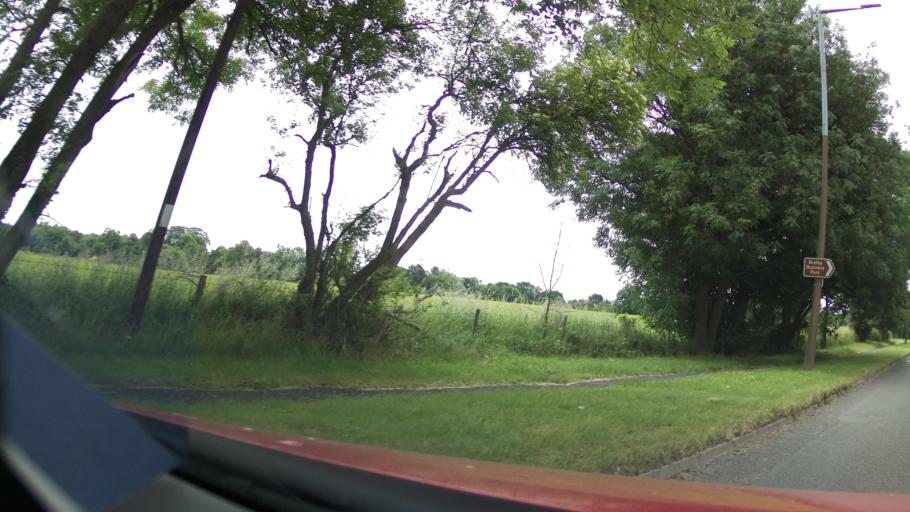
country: GB
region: England
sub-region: Derbyshire
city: Swadlincote
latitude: 52.7940
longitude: -1.5756
